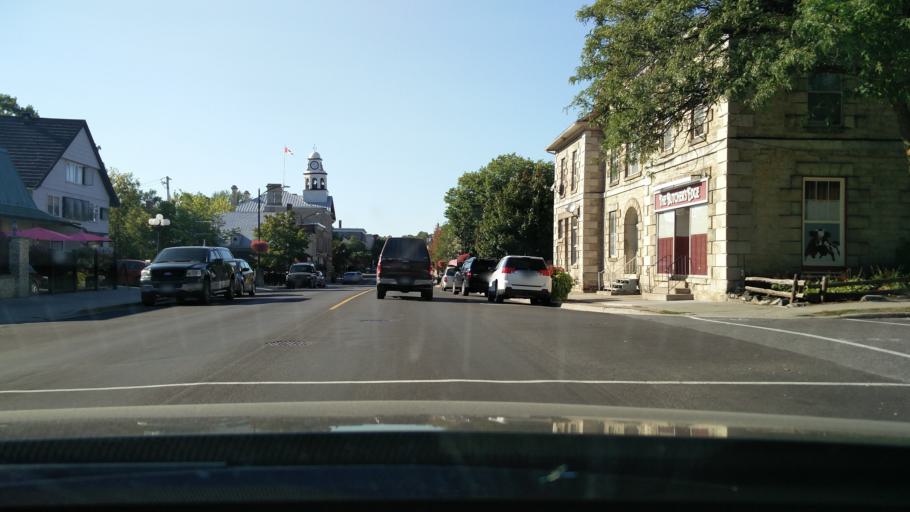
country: CA
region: Ontario
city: Perth
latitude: 44.8981
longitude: -76.2473
